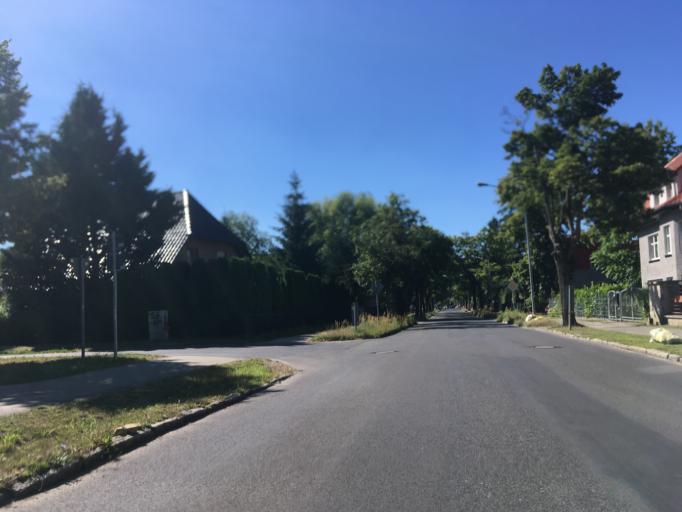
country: DE
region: Brandenburg
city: Petershagen
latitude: 52.5249
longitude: 13.7542
